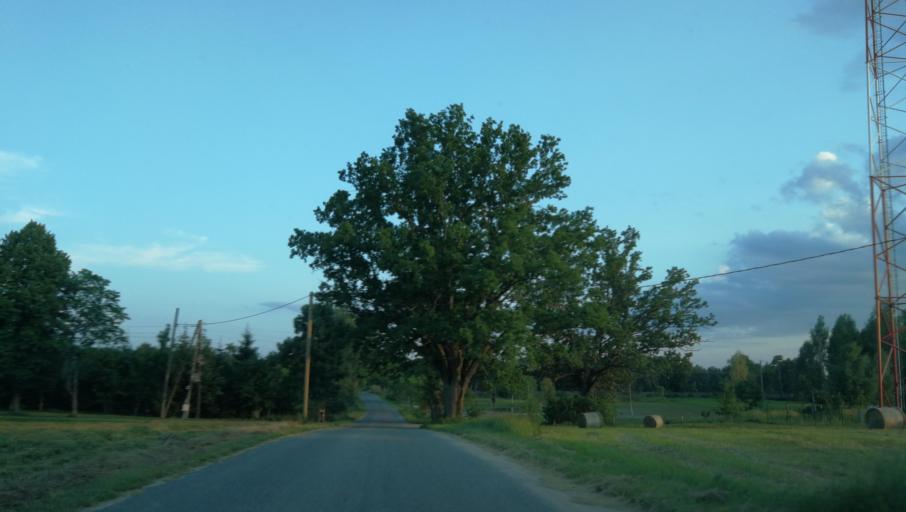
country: LV
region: Amatas Novads
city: Drabesi
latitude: 57.2475
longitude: 25.2145
